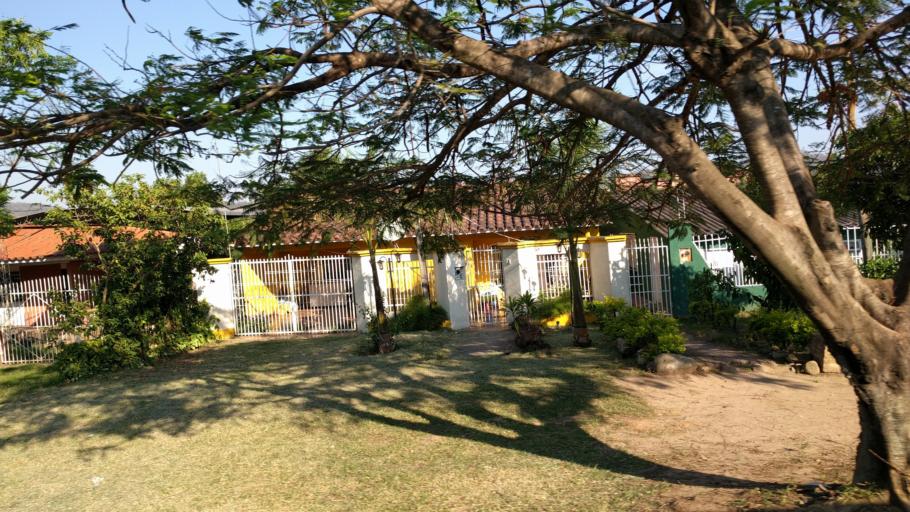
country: BO
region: Santa Cruz
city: Jorochito
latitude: -18.1329
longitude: -63.4716
